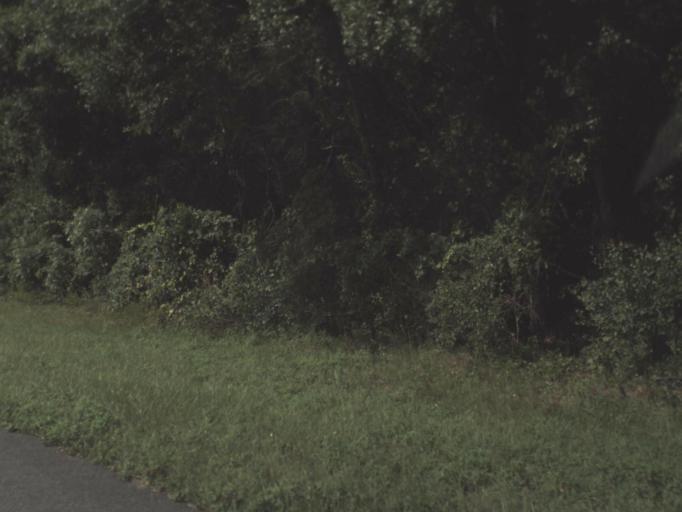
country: US
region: Florida
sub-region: Citrus County
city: Hernando
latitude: 28.9437
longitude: -82.4023
